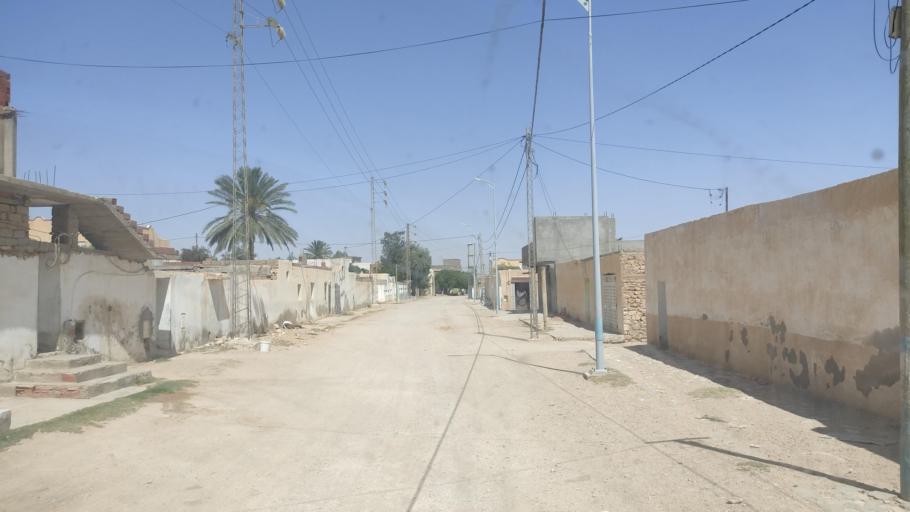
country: TN
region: Gafsa
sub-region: Gafsa Municipality
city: Gafsa
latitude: 34.3369
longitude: 8.9196
